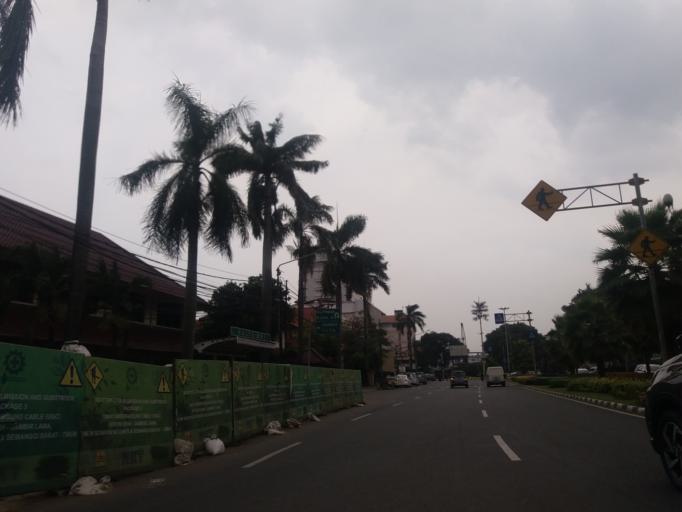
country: ID
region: Jakarta Raya
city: Jakarta
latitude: -6.1869
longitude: 106.8349
